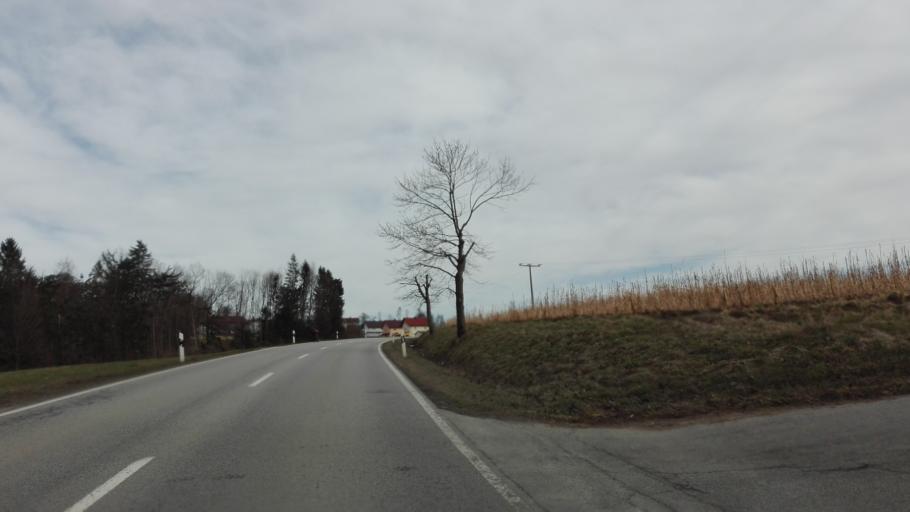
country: DE
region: Bavaria
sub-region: Lower Bavaria
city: Hauzenberg
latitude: 48.6394
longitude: 13.6358
